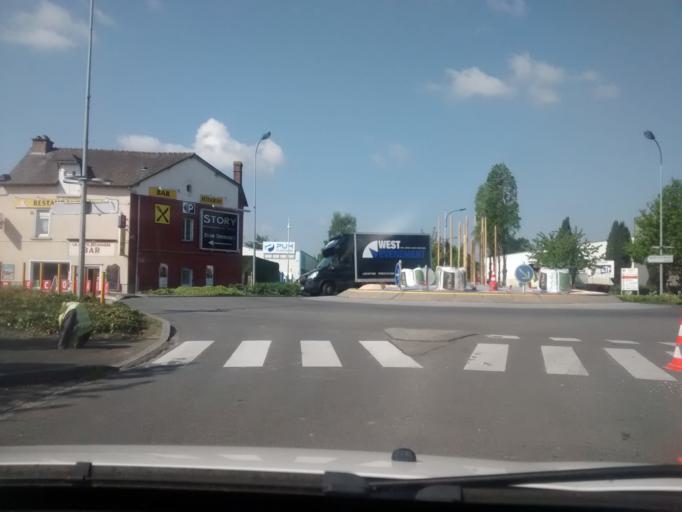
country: FR
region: Brittany
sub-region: Departement d'Ille-et-Vilaine
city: Montgermont
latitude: 48.1557
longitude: -1.7077
